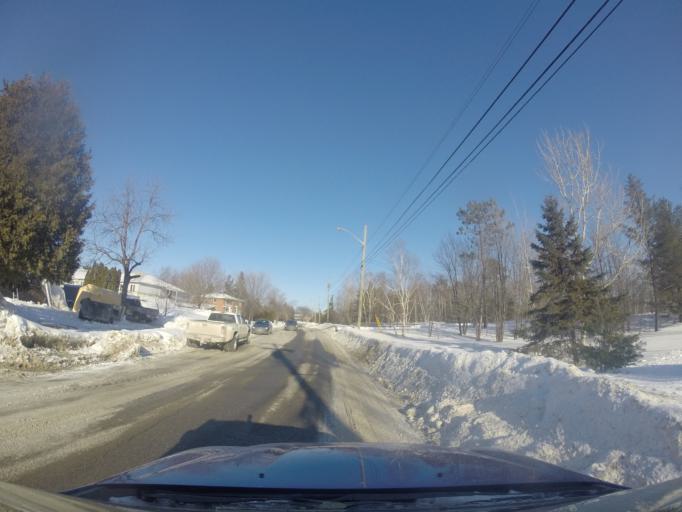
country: CA
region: Ontario
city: Greater Sudbury
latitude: 46.4617
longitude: -80.9966
